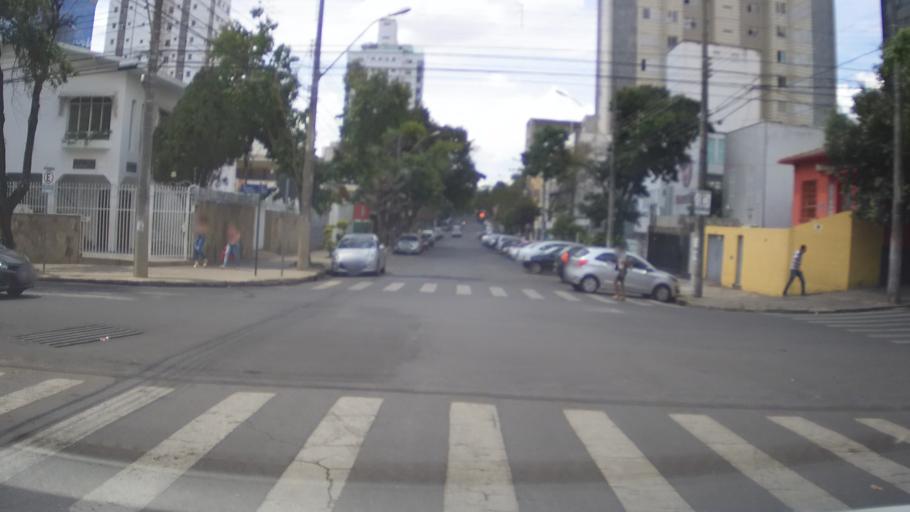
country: BR
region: Minas Gerais
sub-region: Belo Horizonte
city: Belo Horizonte
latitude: -19.9286
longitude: -43.9219
